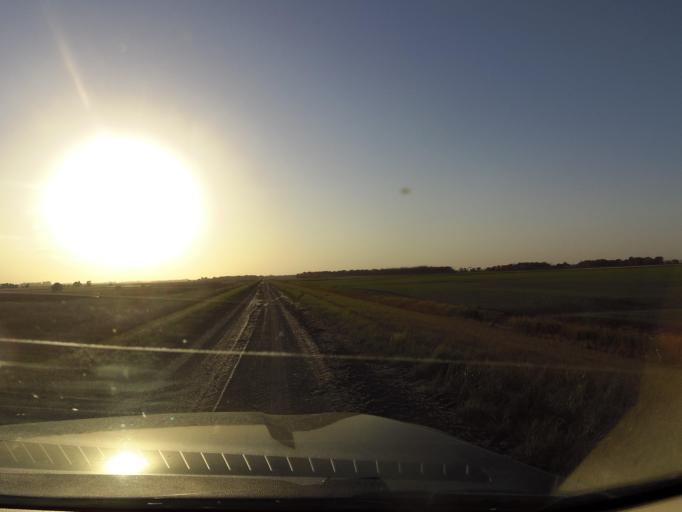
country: US
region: North Dakota
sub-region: Walsh County
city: Grafton
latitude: 48.4199
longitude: -97.4567
